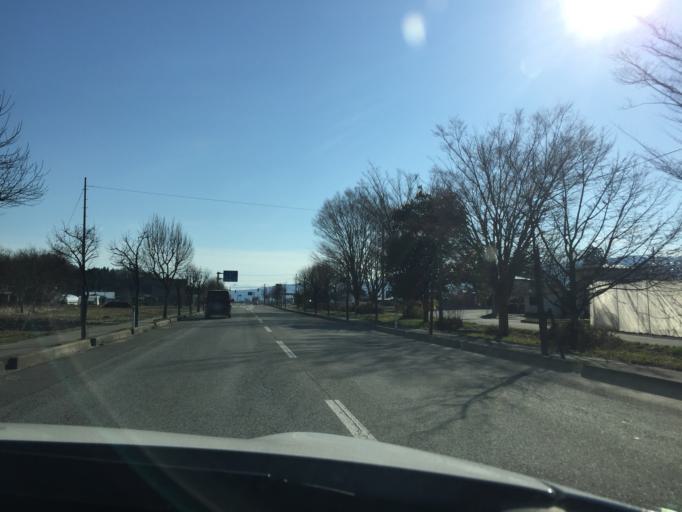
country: JP
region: Yamagata
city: Nagai
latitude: 38.1591
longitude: 140.0737
